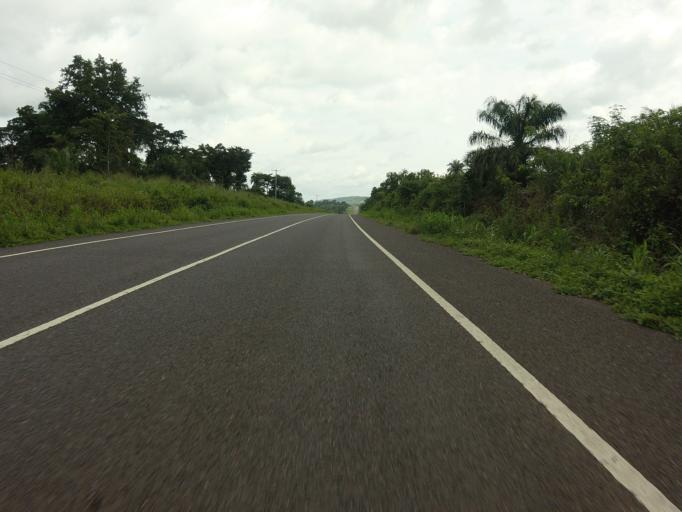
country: TG
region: Plateaux
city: Badou
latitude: 7.9791
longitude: 0.5603
